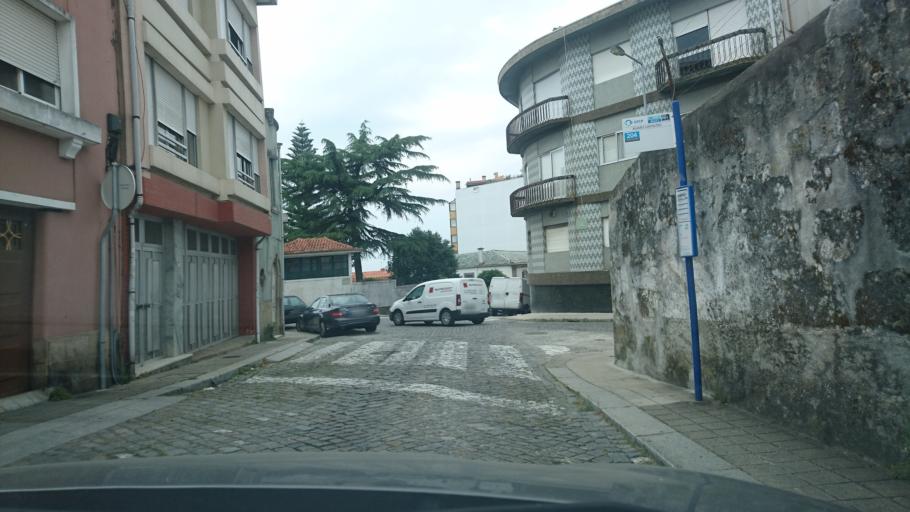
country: PT
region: Porto
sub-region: Porto
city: Porto
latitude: 41.1666
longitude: -8.6017
